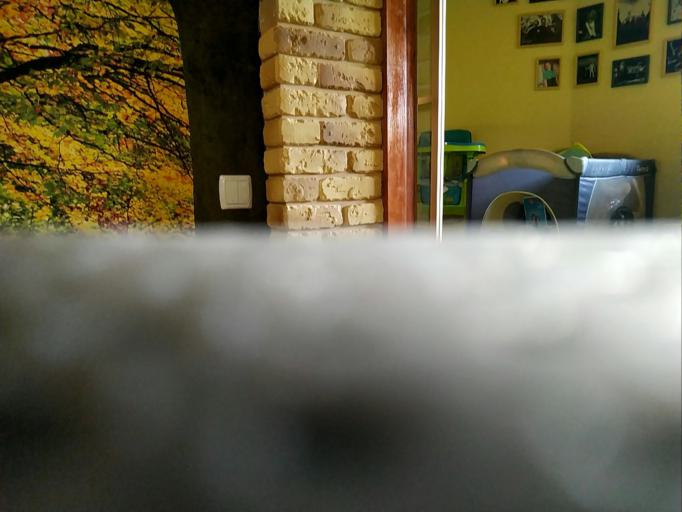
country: RU
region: Kaluga
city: Sukhinichi
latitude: 54.1007
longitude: 35.2792
